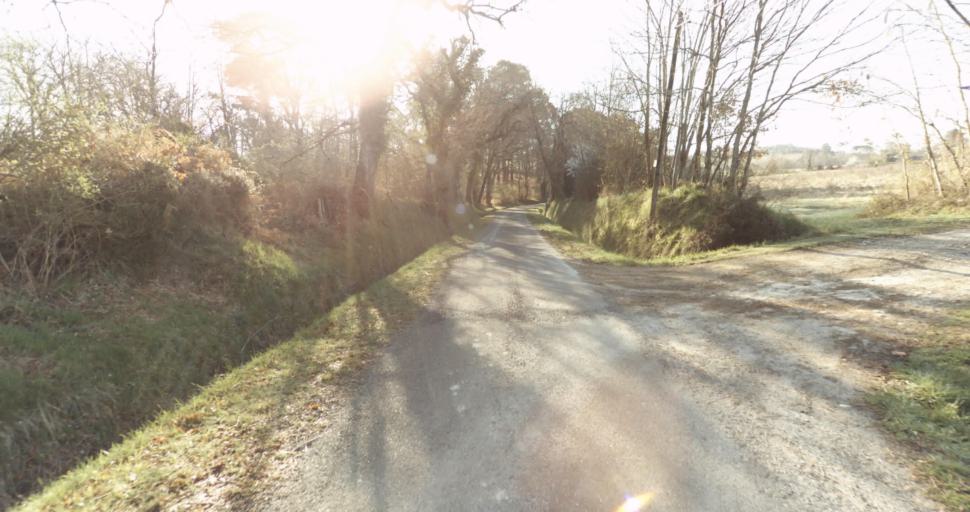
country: FR
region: Midi-Pyrenees
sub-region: Departement du Gers
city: Cazaubon
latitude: 43.9875
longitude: -0.1365
